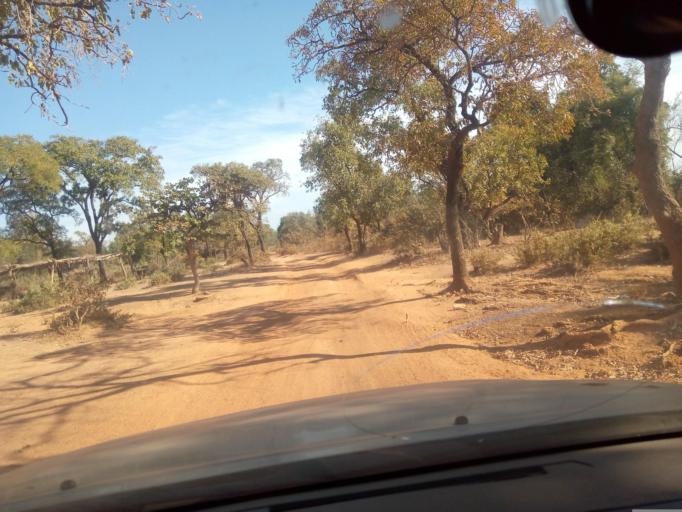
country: ML
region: Sikasso
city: Sikasso
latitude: 11.4674
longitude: -5.3256
